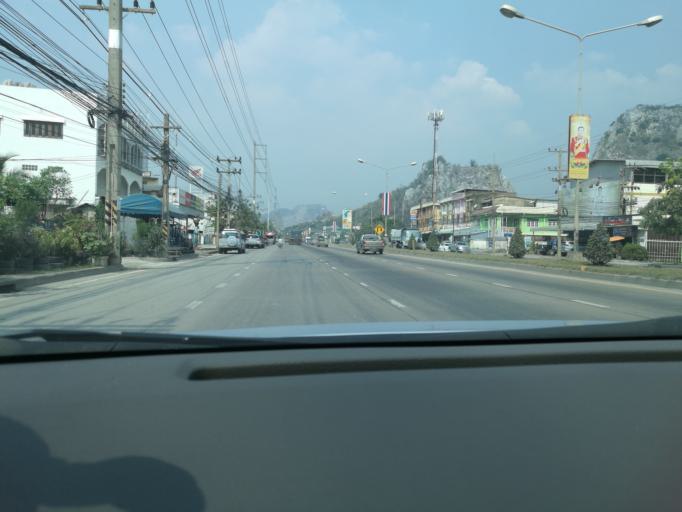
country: TH
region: Sara Buri
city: Phra Phutthabat
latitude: 14.6916
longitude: 100.8687
